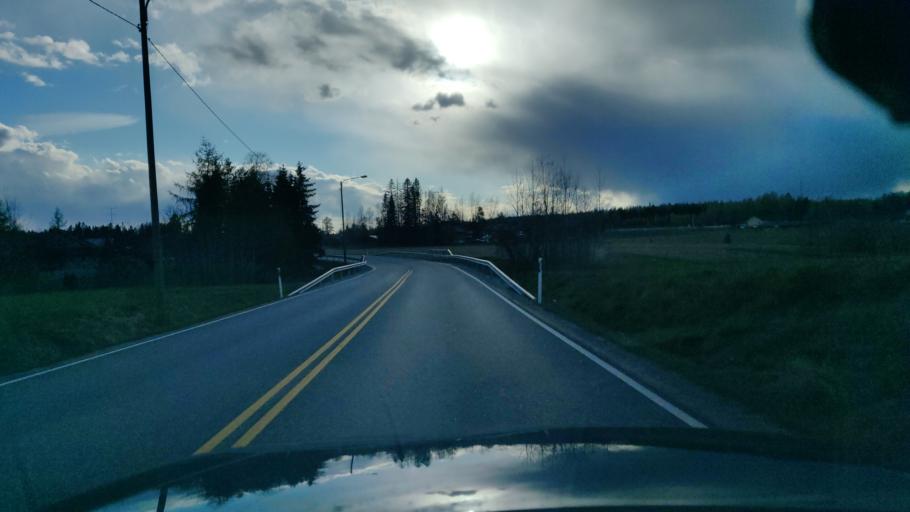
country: FI
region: Uusimaa
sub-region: Helsinki
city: Tuusula
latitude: 60.4543
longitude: 25.0254
